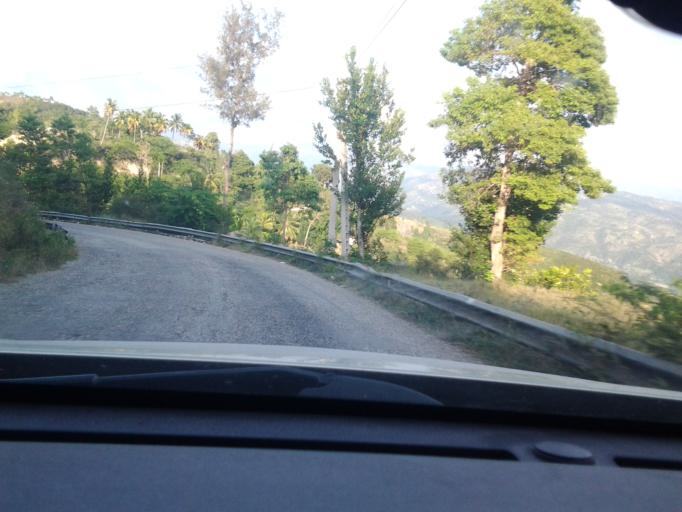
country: HT
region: Sud-Est
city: Jacmel
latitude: 18.3051
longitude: -72.5861
